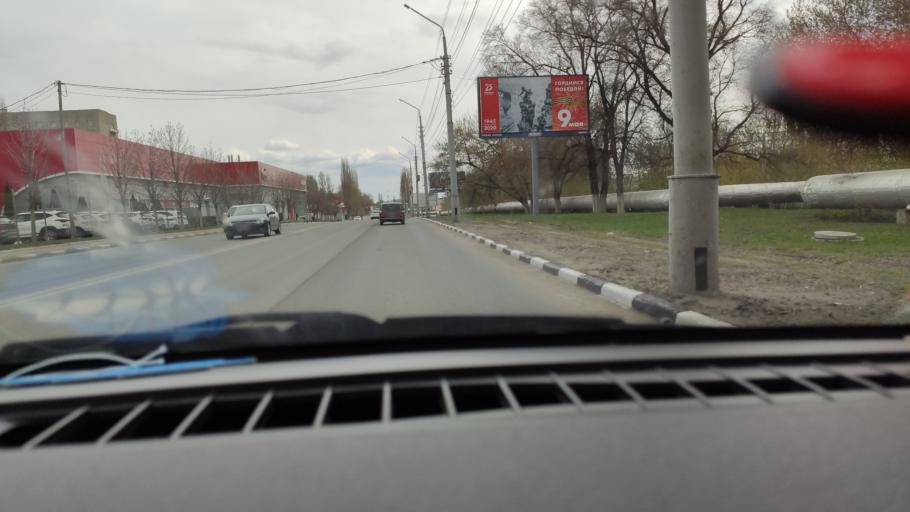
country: RU
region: Saratov
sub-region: Saratovskiy Rayon
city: Saratov
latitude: 51.5689
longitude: 45.9966
